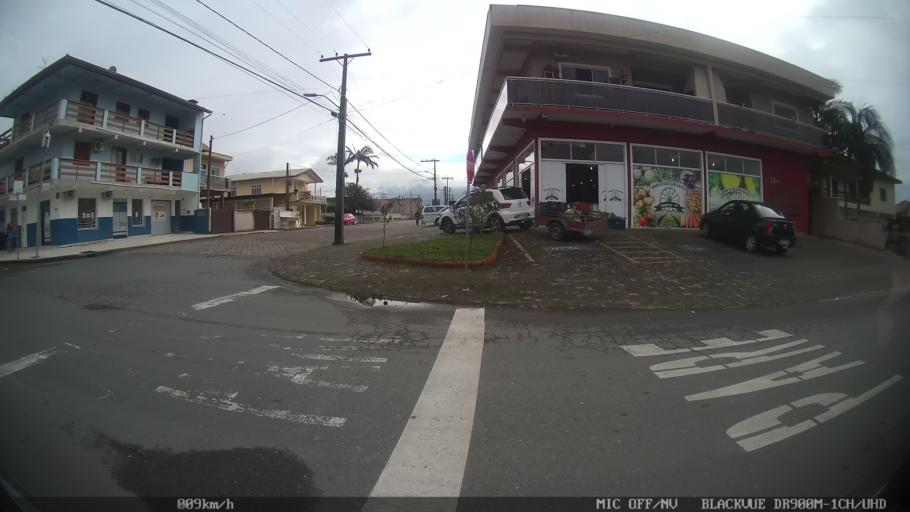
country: BR
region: Santa Catarina
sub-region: Joinville
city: Joinville
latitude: -26.0338
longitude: -48.8530
